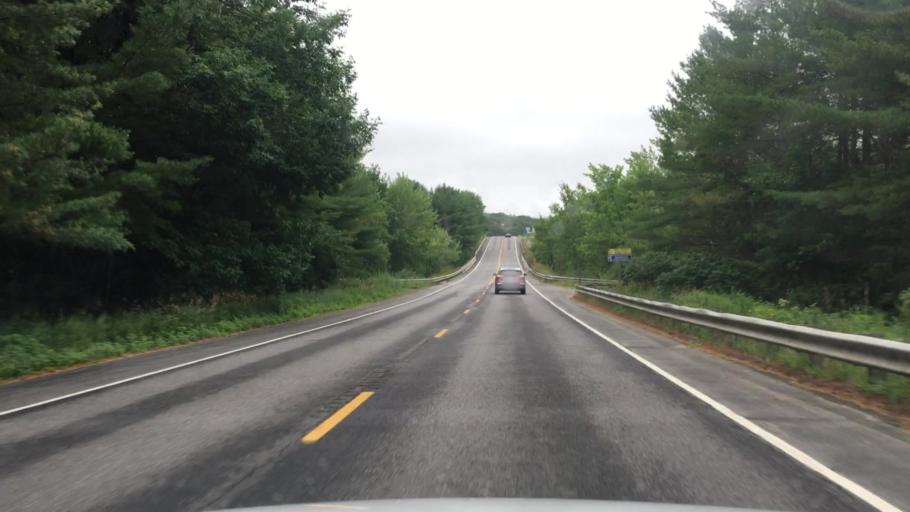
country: US
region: Maine
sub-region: Knox County
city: Union
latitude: 44.2170
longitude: -69.2799
